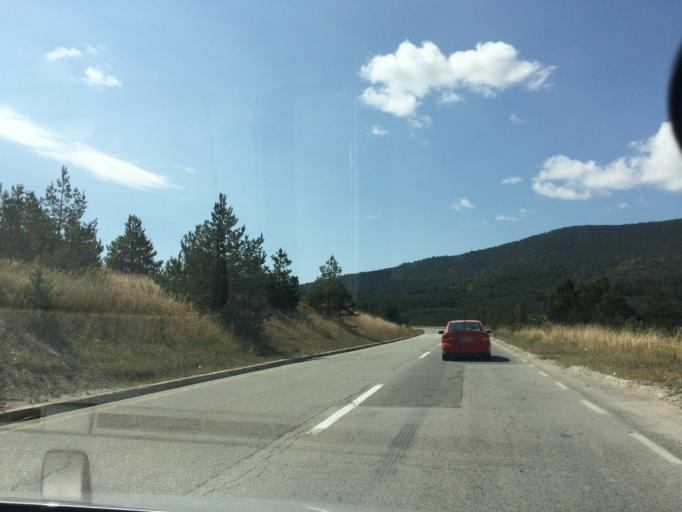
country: RS
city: Zlatibor
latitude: 43.6583
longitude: 19.7076
